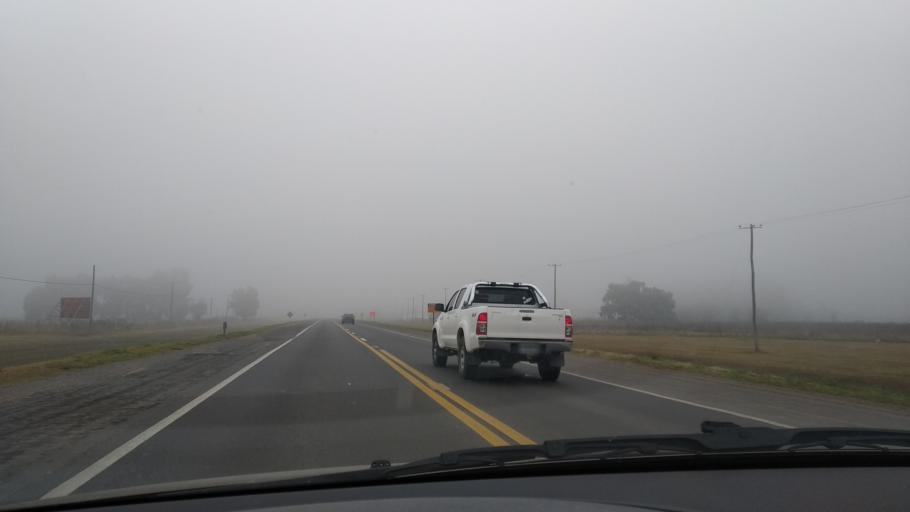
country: AR
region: Buenos Aires
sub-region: Partido de Azul
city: Azul
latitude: -36.8165
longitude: -59.8693
